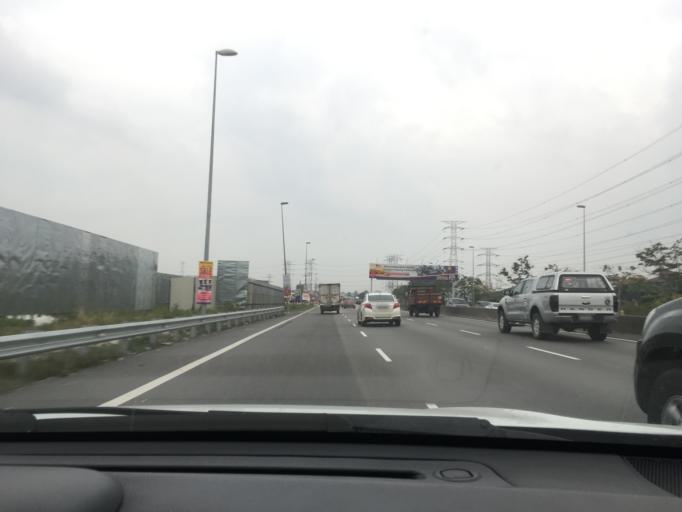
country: MY
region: Selangor
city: Klang
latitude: 3.0976
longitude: 101.4429
